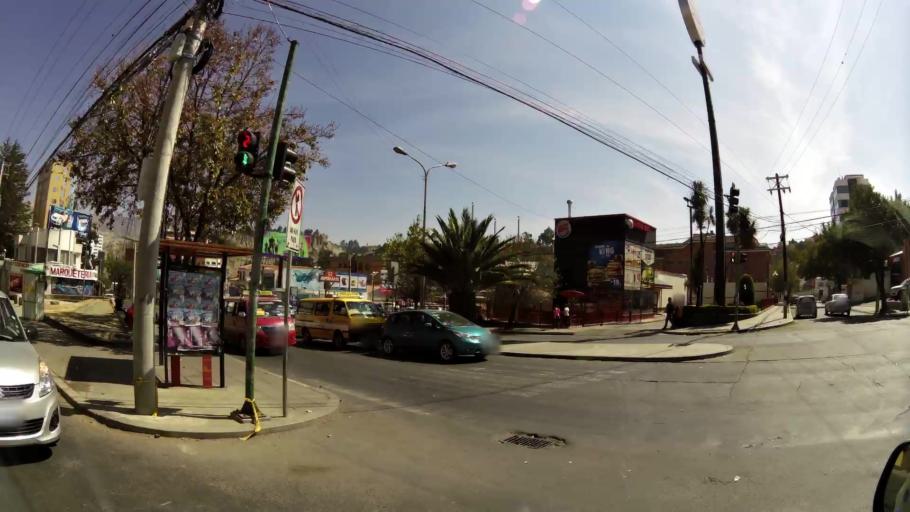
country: BO
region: La Paz
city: La Paz
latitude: -16.5390
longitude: -68.0800
